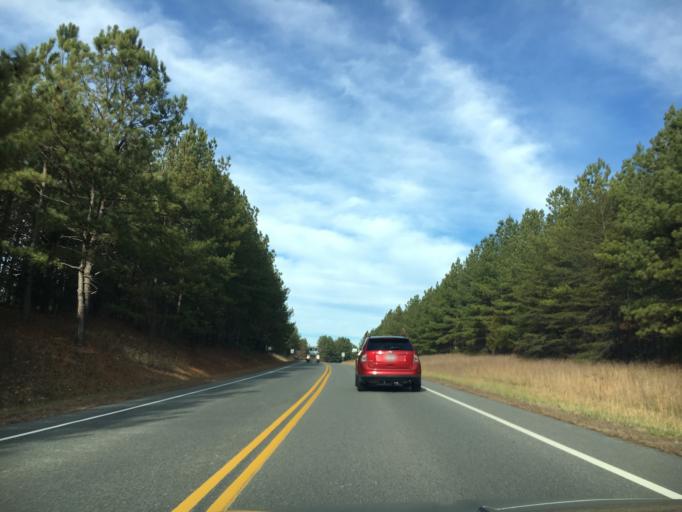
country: US
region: Virginia
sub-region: Louisa County
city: Louisa
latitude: 38.0710
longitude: -77.8807
